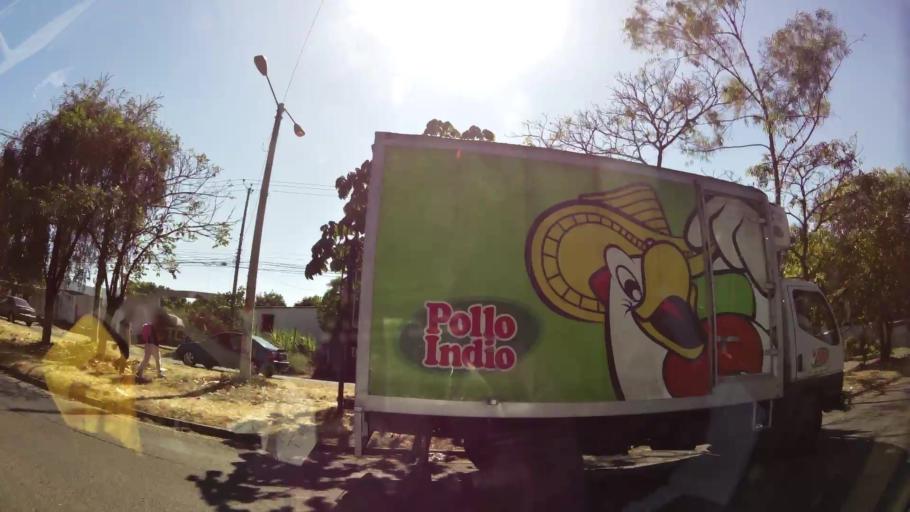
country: SV
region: La Libertad
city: Santa Tecla
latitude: 13.7266
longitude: -89.3758
